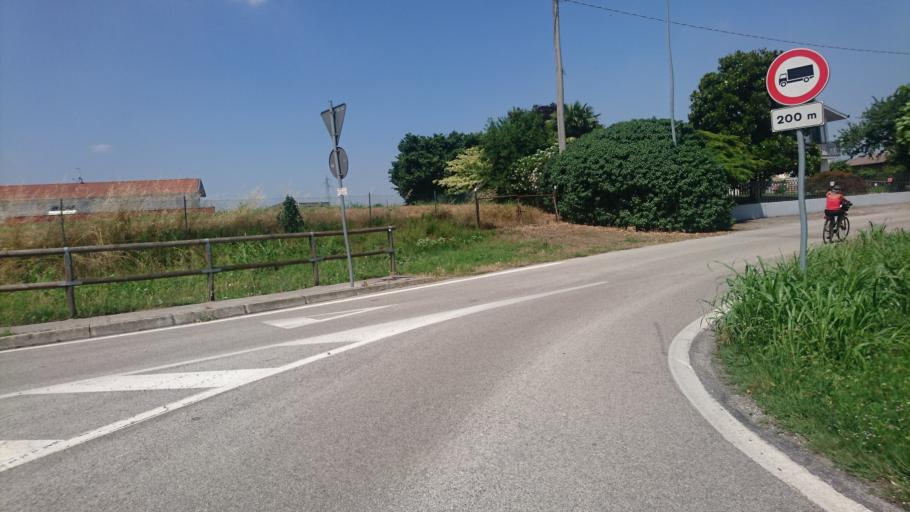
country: IT
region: Veneto
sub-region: Provincia di Venezia
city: Galta
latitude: 45.3950
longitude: 12.0202
